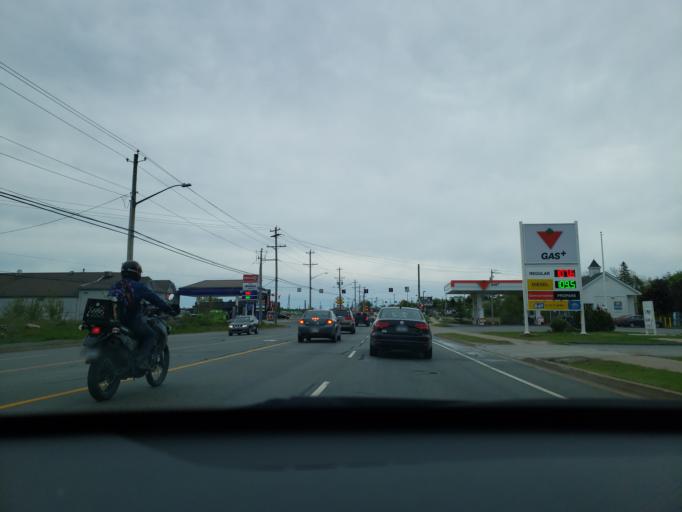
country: CA
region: Nova Scotia
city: Cole Harbour
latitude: 44.6928
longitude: -63.5017
